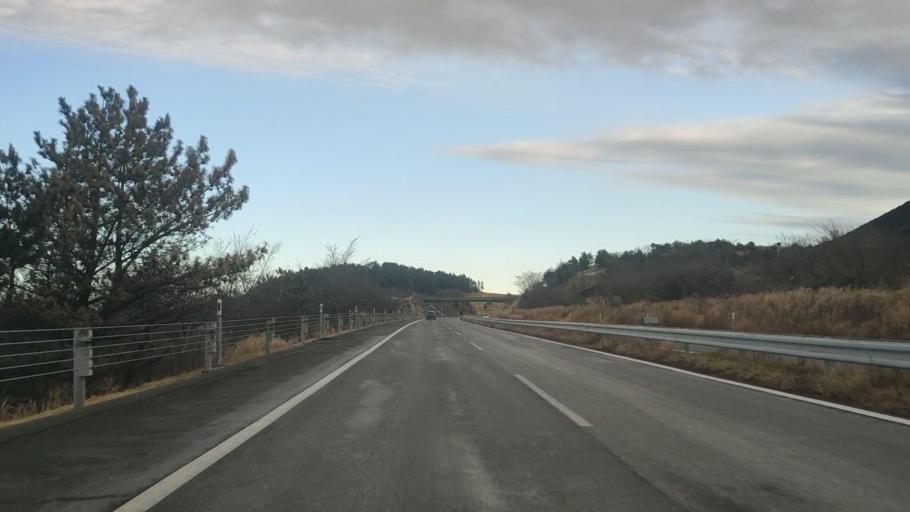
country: JP
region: Oita
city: Beppu
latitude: 33.3116
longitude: 131.4076
